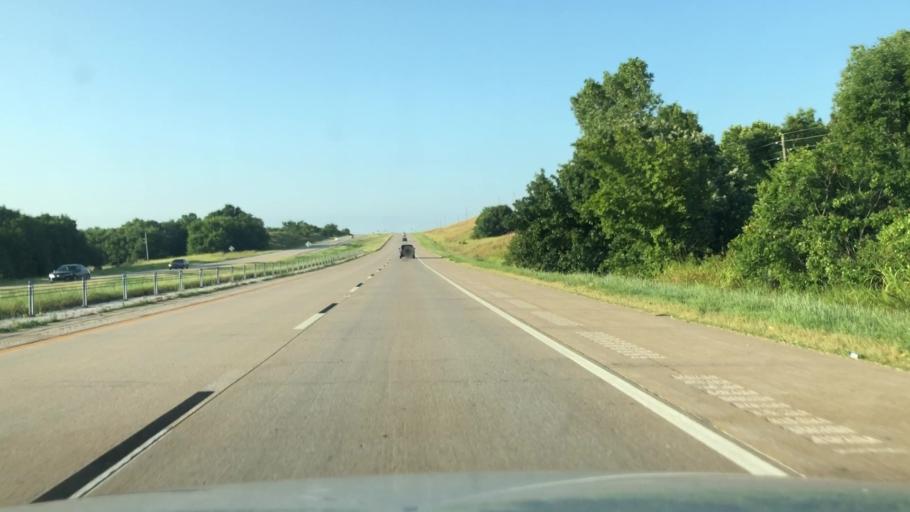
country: US
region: Oklahoma
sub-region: Osage County
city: Skiatook
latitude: 36.4869
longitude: -95.9207
